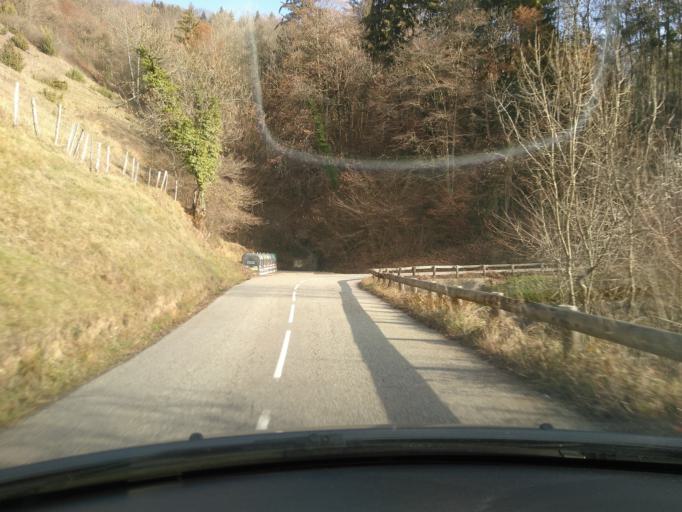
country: FR
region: Rhone-Alpes
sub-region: Departement de l'Isere
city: Villard-Bonnot
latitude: 45.2403
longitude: 5.9151
